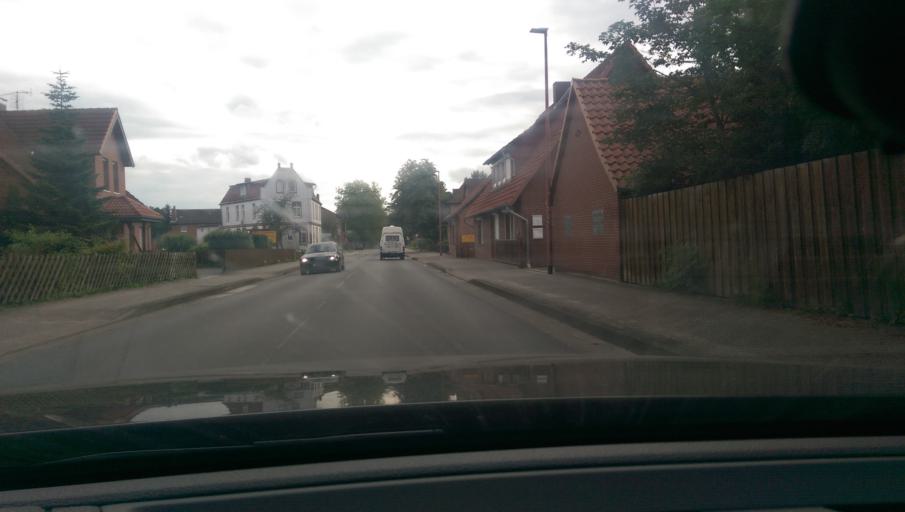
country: DE
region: Lower Saxony
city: Winsen (Aller)
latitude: 52.6751
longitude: 9.9078
